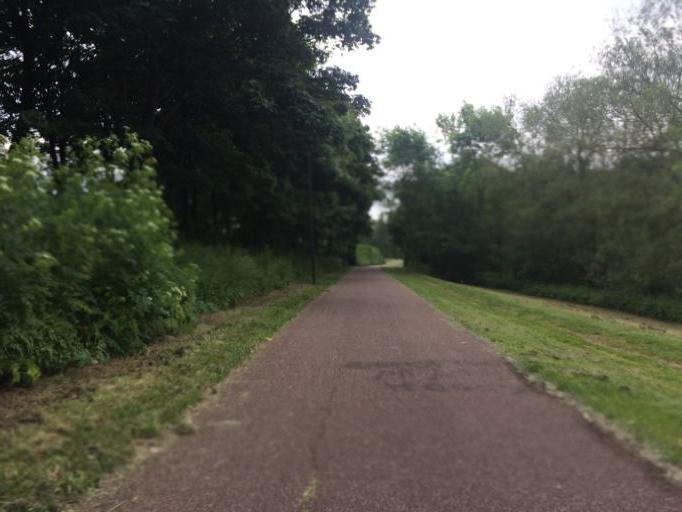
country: GB
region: England
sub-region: Milton Keynes
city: Milton Keynes
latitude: 52.0275
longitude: -0.7677
